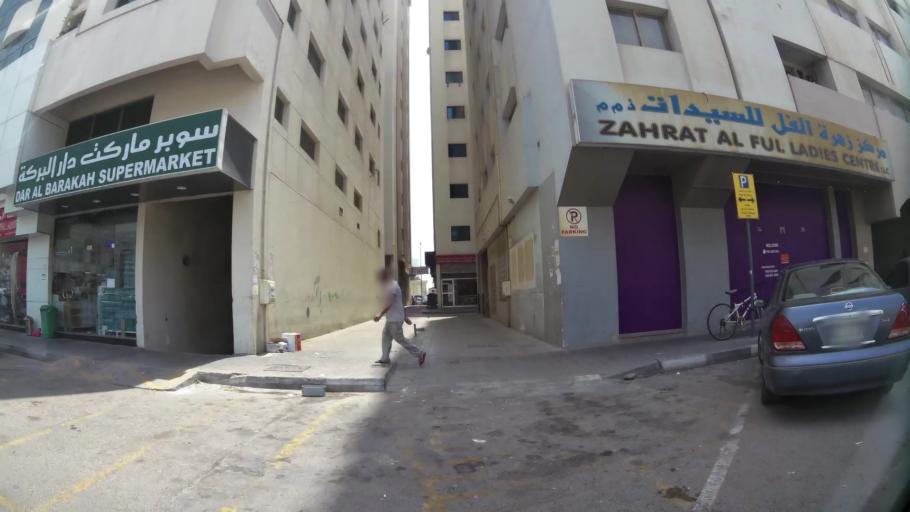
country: AE
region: Ash Shariqah
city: Sharjah
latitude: 25.3331
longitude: 55.3913
